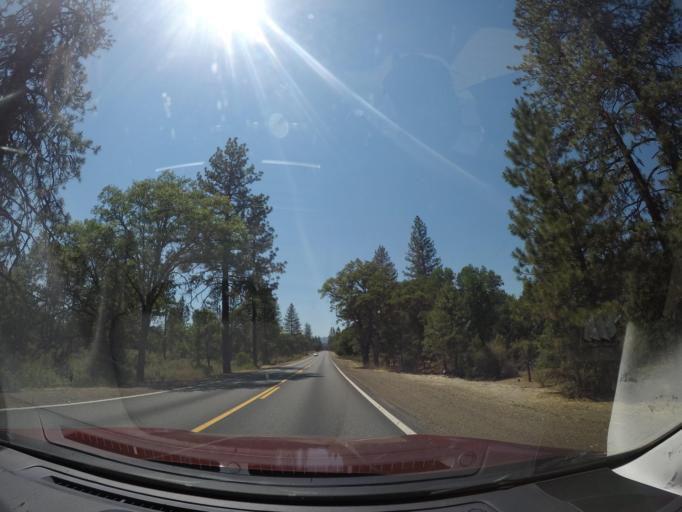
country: US
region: California
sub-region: Shasta County
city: Burney
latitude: 40.9833
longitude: -121.5247
